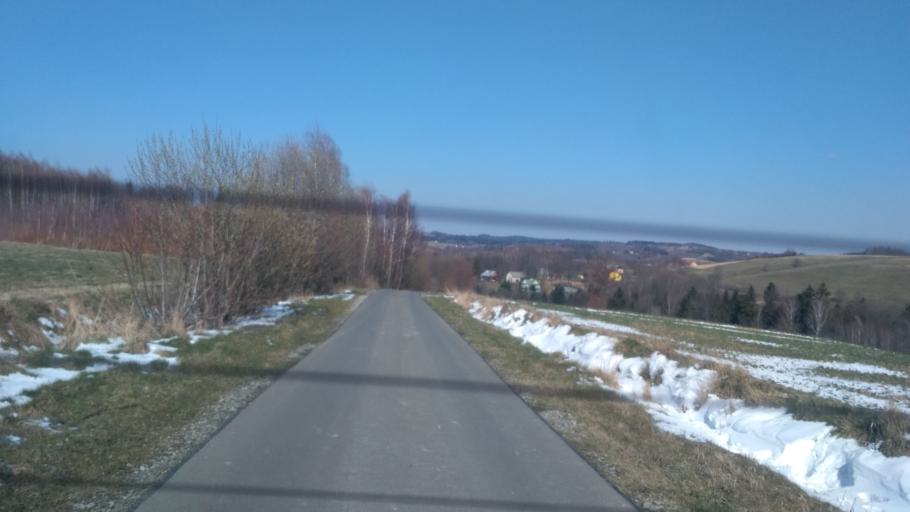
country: PL
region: Subcarpathian Voivodeship
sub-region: Powiat strzyzowski
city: Gwoznica Gorna
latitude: 49.8229
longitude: 22.0086
